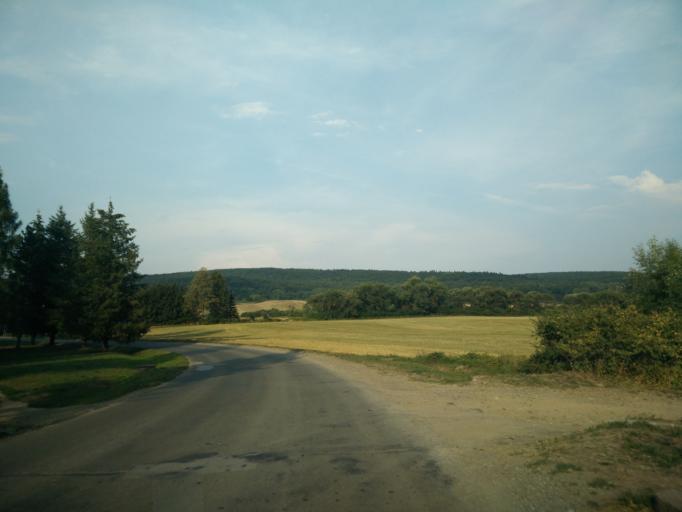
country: SK
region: Banskobystricky
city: Ziar nad Hronom
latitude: 48.6084
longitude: 18.8400
